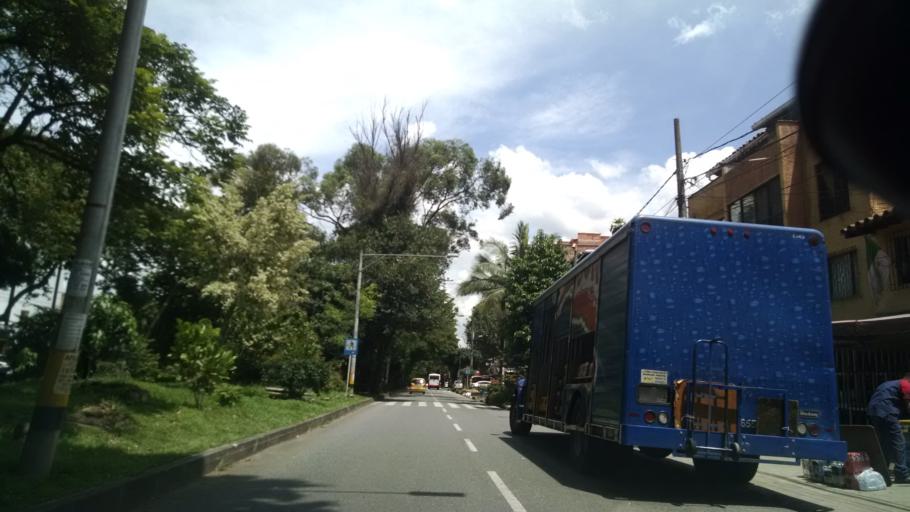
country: CO
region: Antioquia
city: Itagui
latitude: 6.2088
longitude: -75.5886
